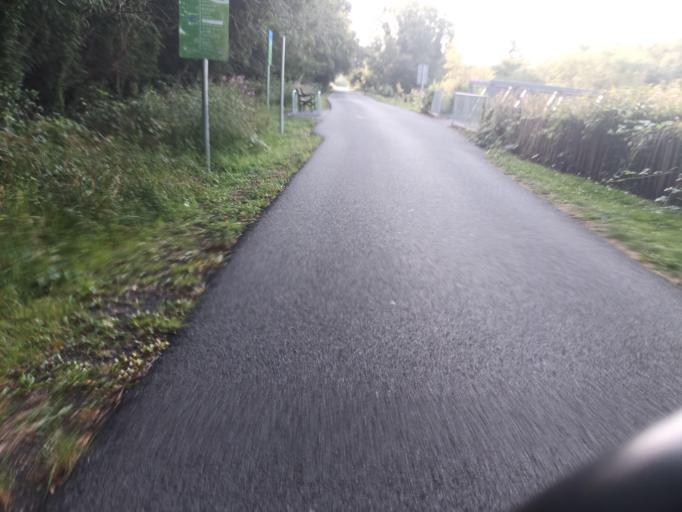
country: GB
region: Northern Ireland
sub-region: Castlereagh District
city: Dundonald
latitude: 54.5899
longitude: -5.8192
